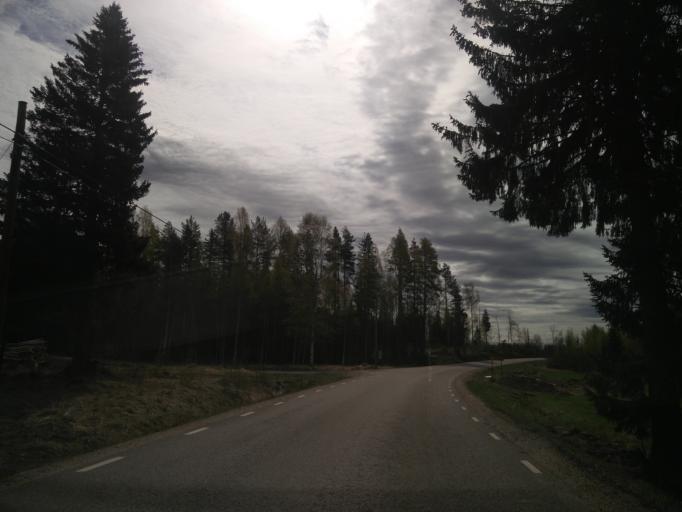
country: SE
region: Vaesternorrland
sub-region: Sundsvalls Kommun
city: Vi
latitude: 62.2347
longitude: 17.1281
